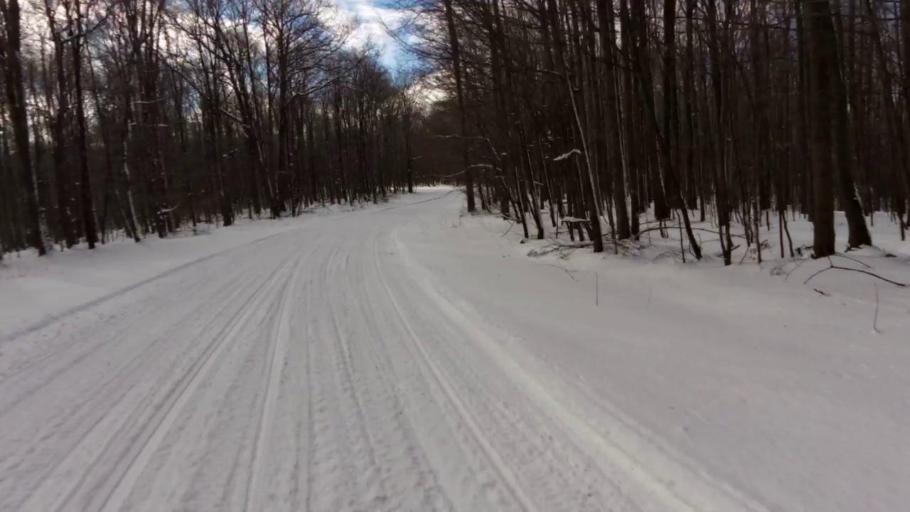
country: US
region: Pennsylvania
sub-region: McKean County
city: Bradford
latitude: 42.0348
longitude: -78.7079
